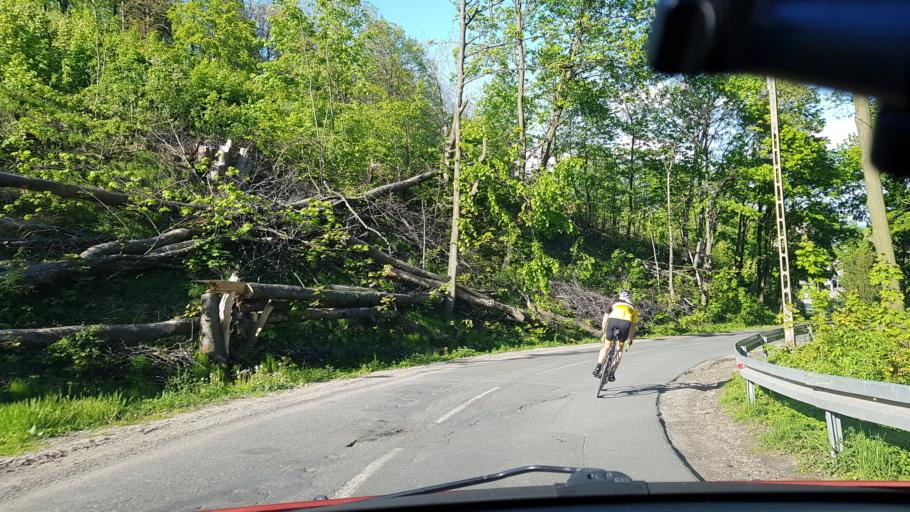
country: PL
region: Lower Silesian Voivodeship
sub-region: Powiat zabkowicki
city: Budzow
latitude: 50.5753
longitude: 16.6523
